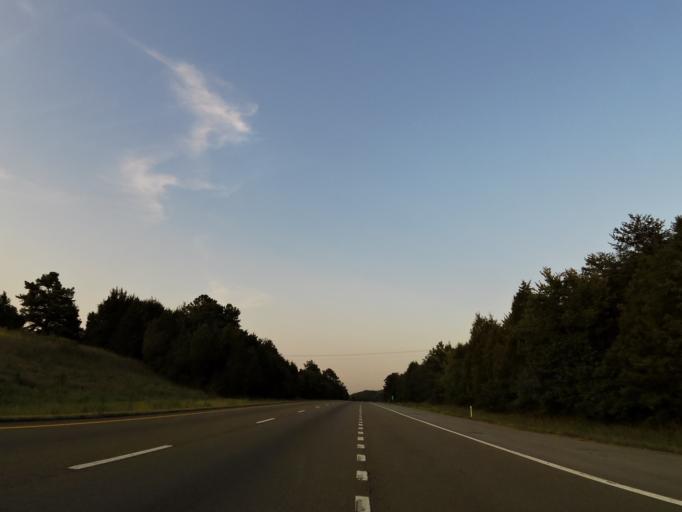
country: US
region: Tennessee
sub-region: Loudon County
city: Loudon
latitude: 35.7861
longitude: -84.3387
